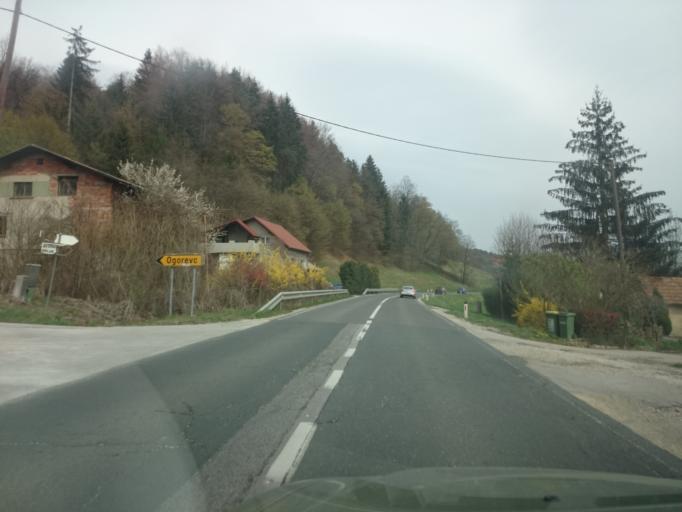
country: SI
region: Store
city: Store
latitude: 46.2205
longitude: 15.3435
